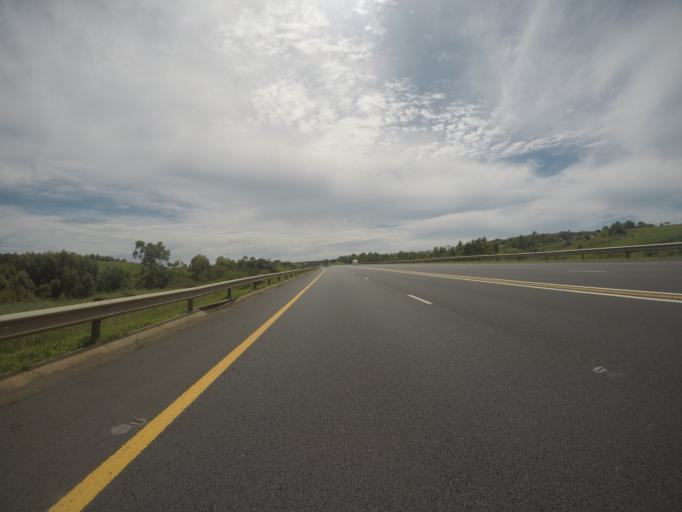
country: ZA
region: KwaZulu-Natal
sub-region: iLembe District Municipality
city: Mandeni
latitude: -29.1647
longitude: 31.5296
